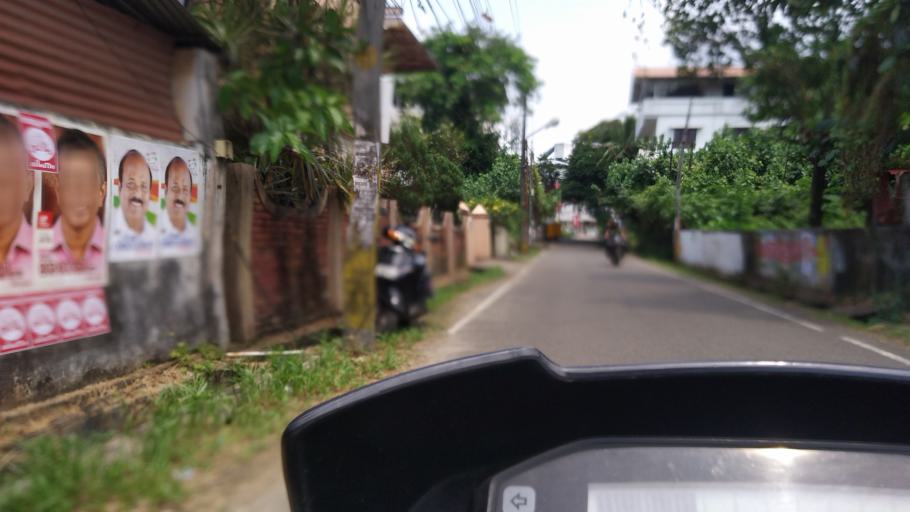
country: IN
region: Kerala
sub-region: Ernakulam
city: Cochin
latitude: 9.9706
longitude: 76.2923
